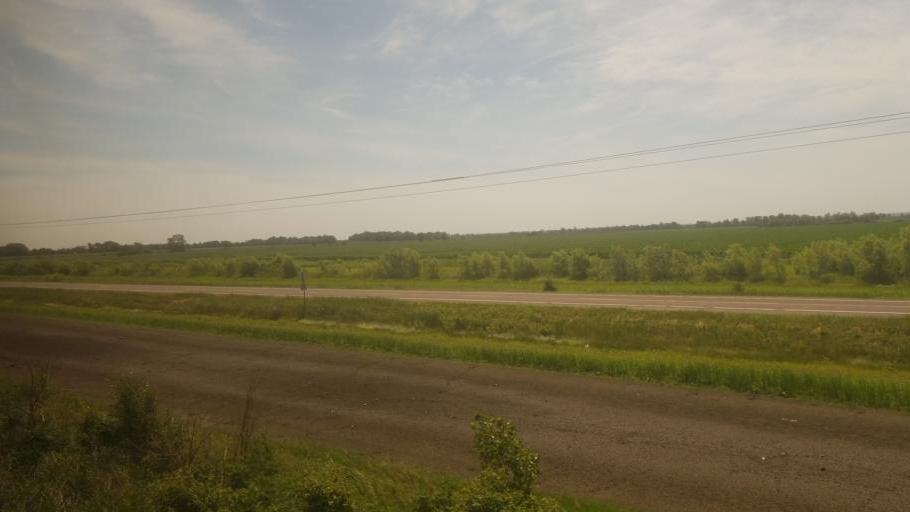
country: US
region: Missouri
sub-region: Carroll County
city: Carrollton
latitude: 39.3123
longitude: -93.6358
